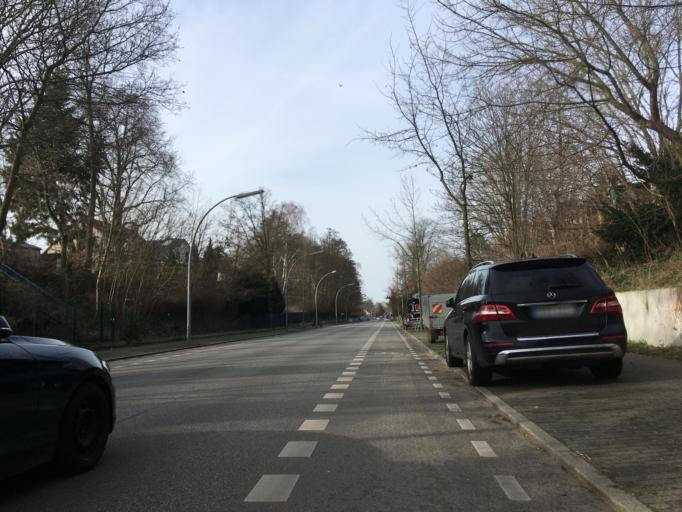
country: DE
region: Berlin
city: Lubars
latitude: 52.6125
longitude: 13.3582
